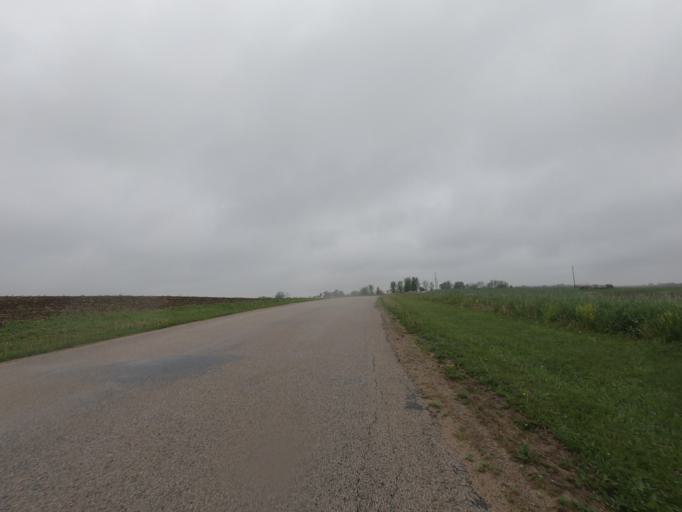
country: US
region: Wisconsin
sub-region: Grant County
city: Hazel Green
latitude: 42.4918
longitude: -90.4957
